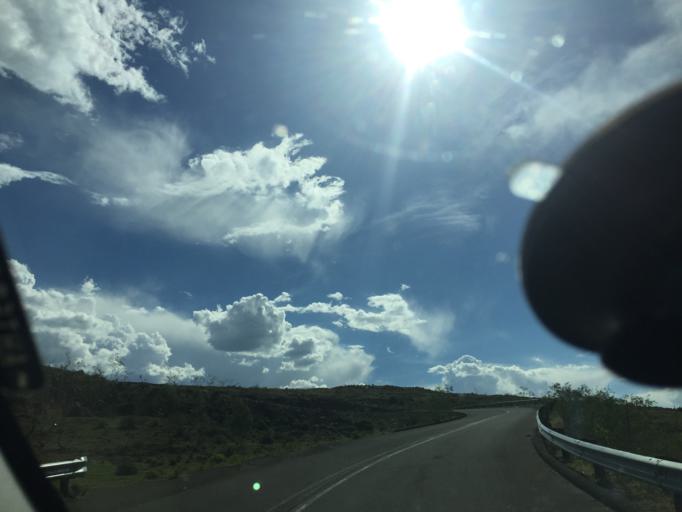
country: LS
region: Maseru
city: Nako
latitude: -29.6470
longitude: 27.7630
